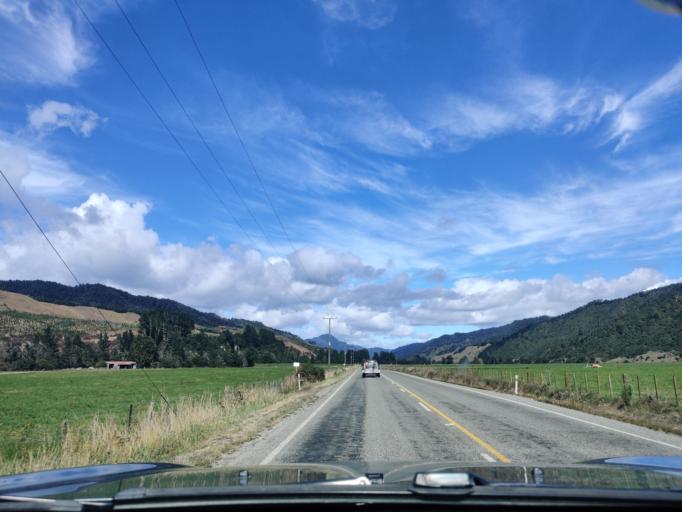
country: NZ
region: Tasman
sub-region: Tasman District
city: Wakefield
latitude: -41.7039
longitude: 172.4249
